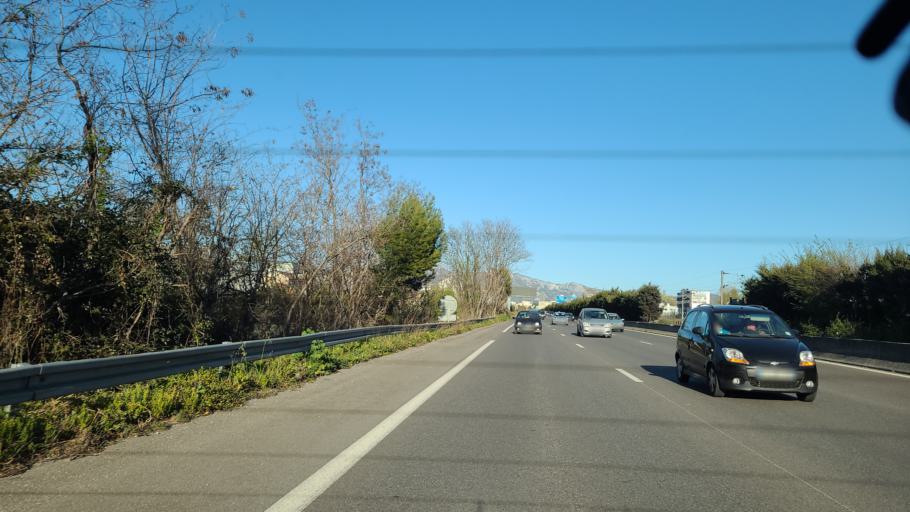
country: FR
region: Provence-Alpes-Cote d'Azur
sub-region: Departement des Bouches-du-Rhone
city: La Penne-sur-Huveaune
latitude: 43.2859
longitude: 5.5284
